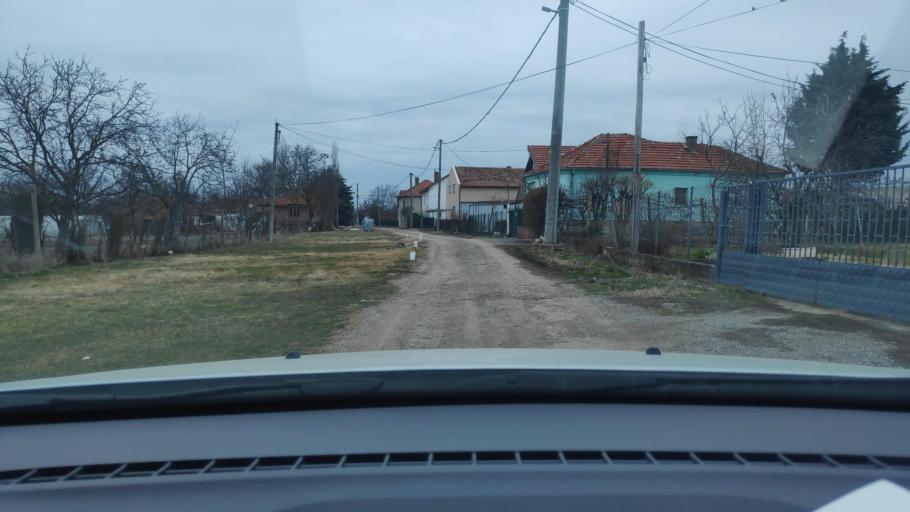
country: MK
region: Opstina Lipkovo
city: Matejche
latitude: 42.0852
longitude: 21.6198
